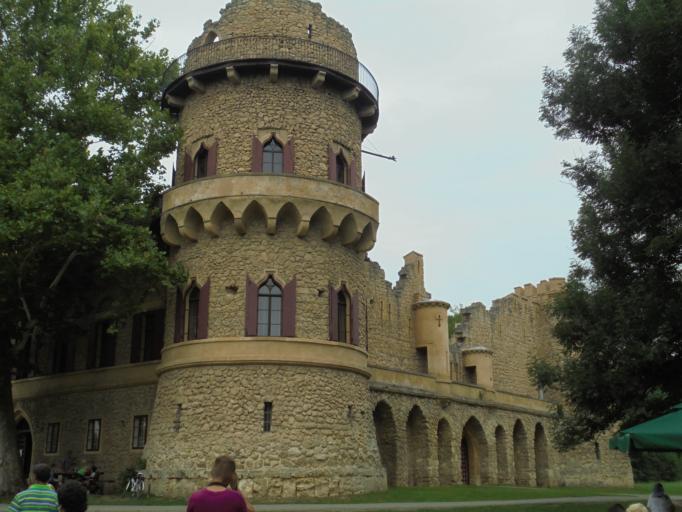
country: CZ
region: South Moravian
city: Podivin
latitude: 48.8047
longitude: 16.8330
